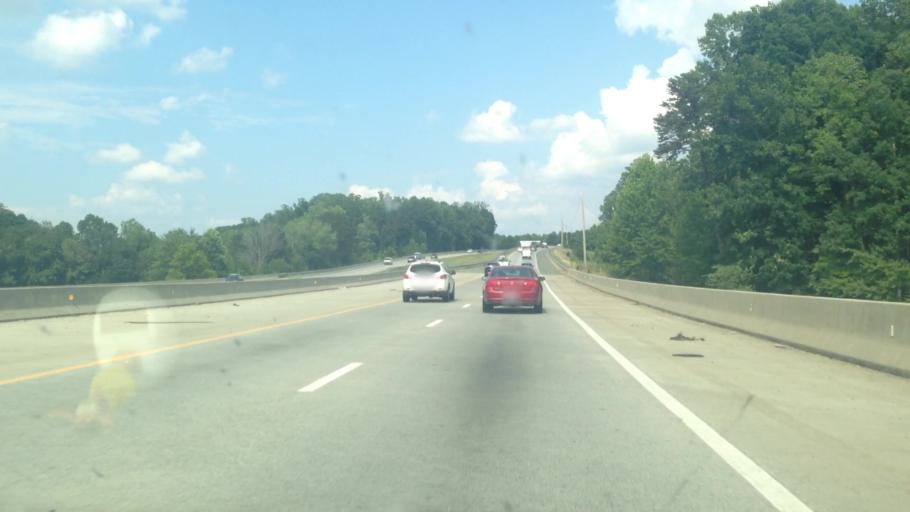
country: US
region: North Carolina
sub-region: Forsyth County
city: Winston-Salem
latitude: 36.1048
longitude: -80.1865
